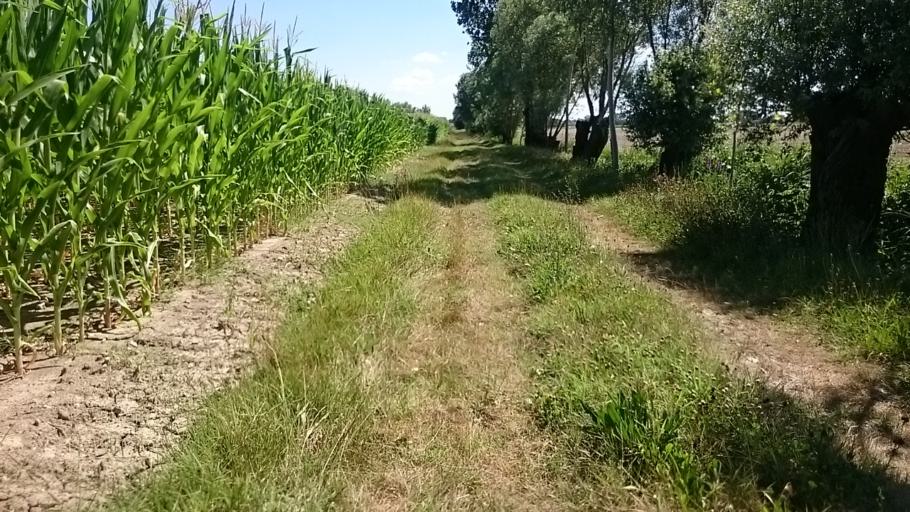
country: IT
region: Veneto
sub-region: Provincia di Venezia
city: Fiesso d'Artico
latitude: 45.4341
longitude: 12.0222
